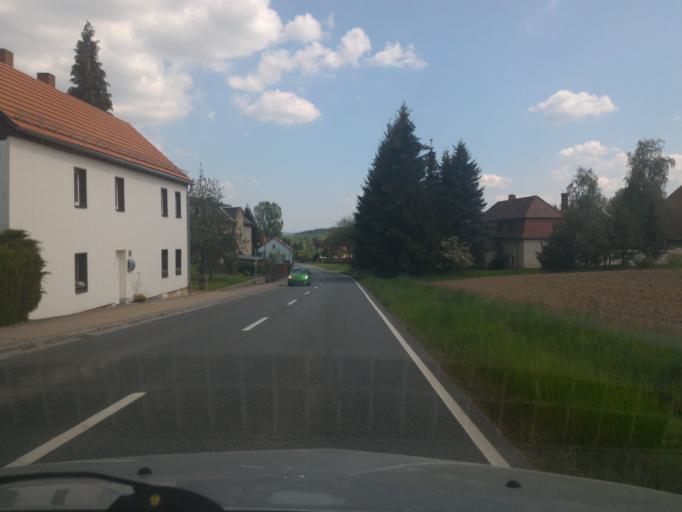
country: DE
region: Saxony
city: Bertsdorf-Hoernitz
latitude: 50.9013
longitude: 14.7428
